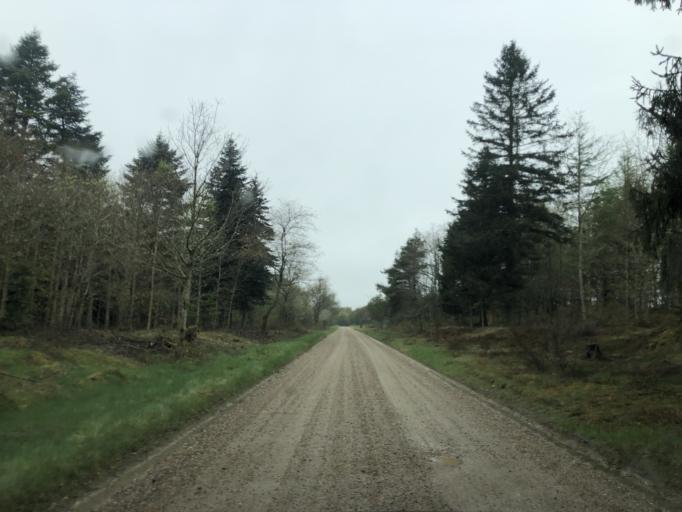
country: DK
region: Central Jutland
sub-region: Lemvig Kommune
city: Lemvig
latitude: 56.4814
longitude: 8.3673
